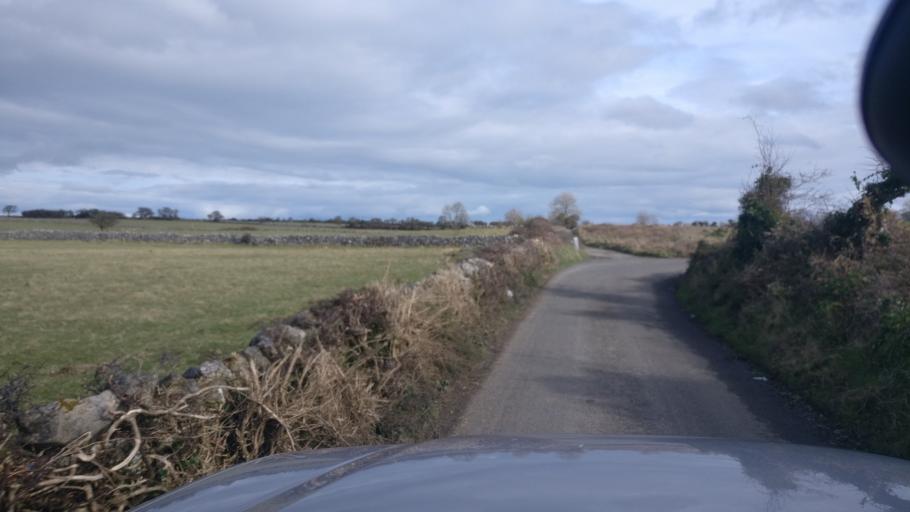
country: IE
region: Connaught
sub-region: County Galway
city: Loughrea
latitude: 53.1968
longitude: -8.5408
